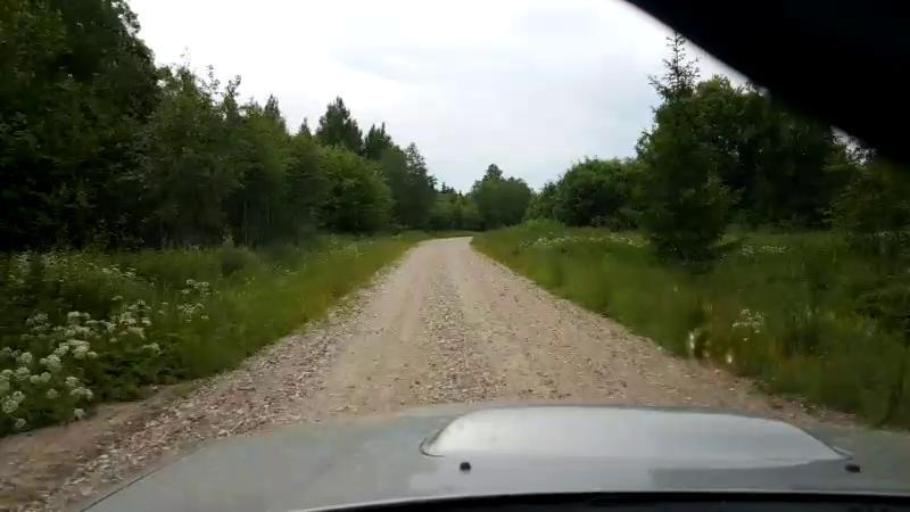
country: EE
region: Paernumaa
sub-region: Tootsi vald
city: Tootsi
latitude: 58.5442
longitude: 24.7373
